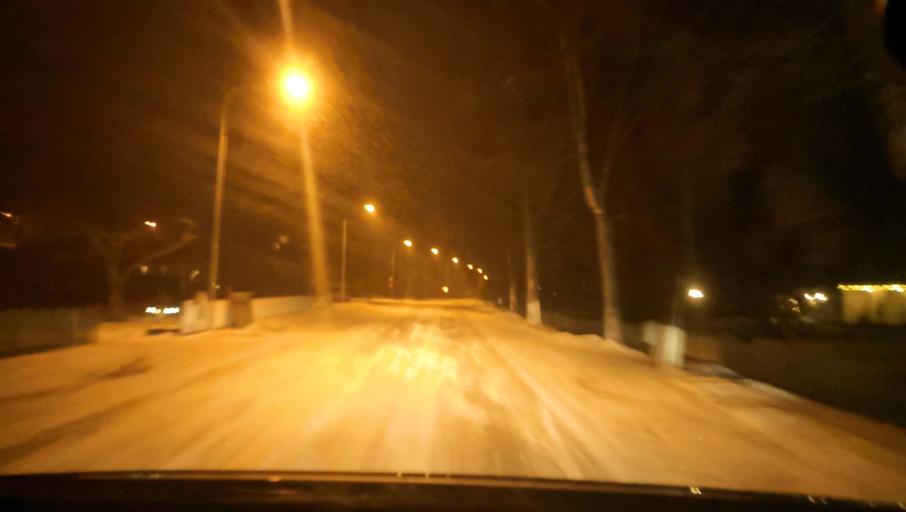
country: SE
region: Uppsala
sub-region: Heby Kommun
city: Tarnsjo
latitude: 60.1496
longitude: 16.9206
